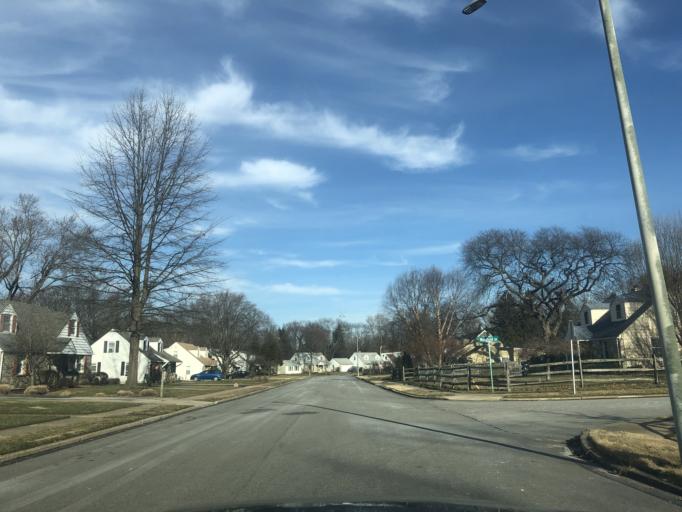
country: US
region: Pennsylvania
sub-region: Montgomery County
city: Flourtown
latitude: 40.1064
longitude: -75.2024
